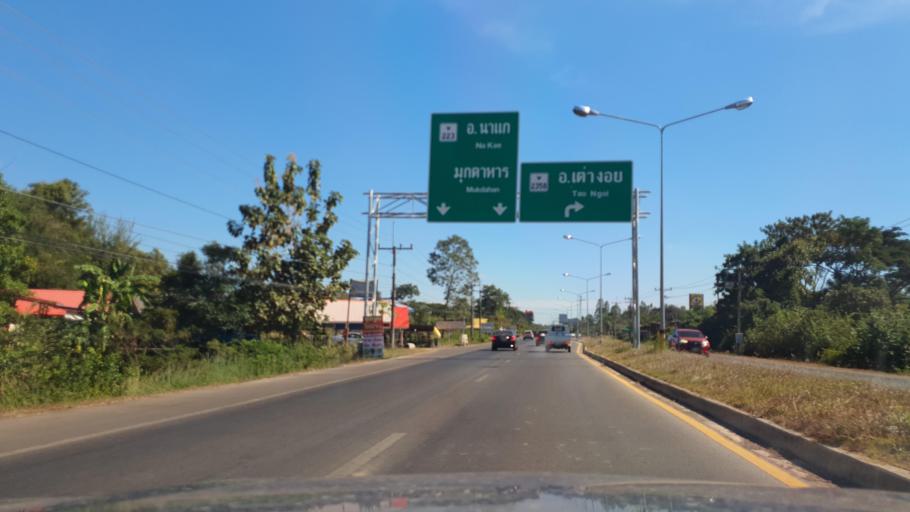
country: TH
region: Sakon Nakhon
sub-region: Amphoe Khok Si Suphan
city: Khok Si Suphan
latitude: 17.0708
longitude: 104.2133
